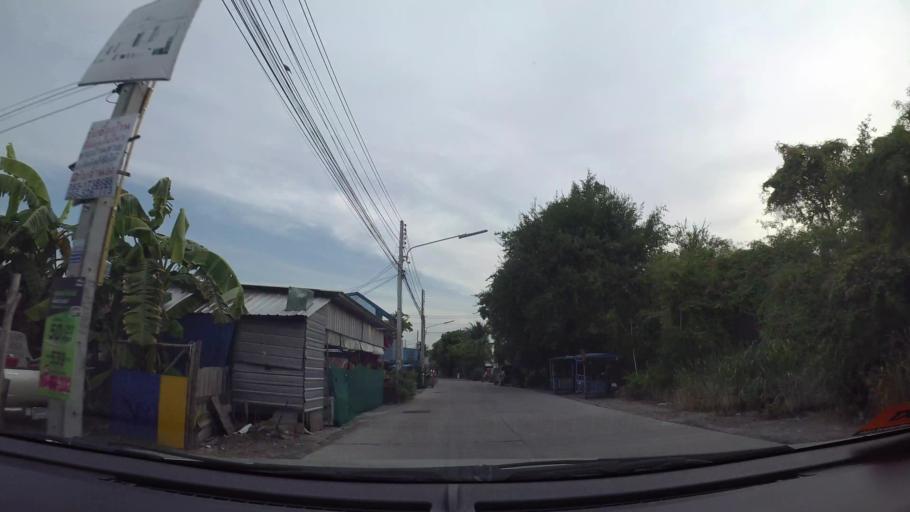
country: TH
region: Chon Buri
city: Chon Buri
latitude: 13.3392
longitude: 100.9838
